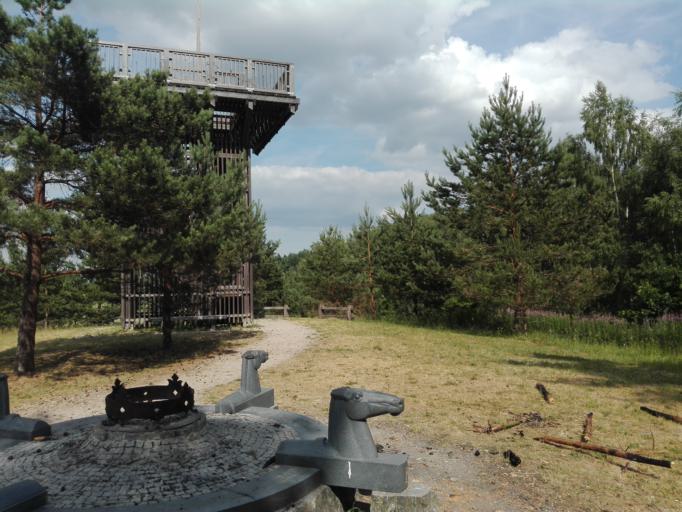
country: LT
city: Skaidiskes
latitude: 54.5268
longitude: 25.6259
